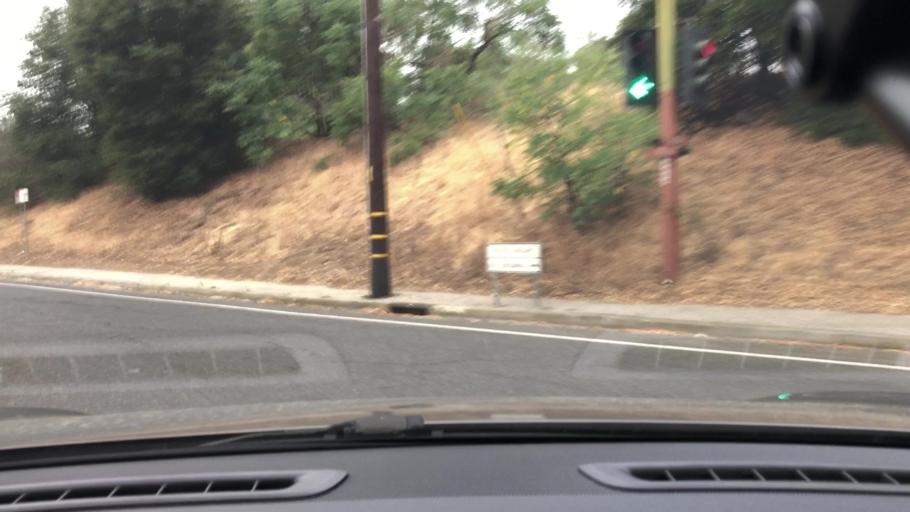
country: US
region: California
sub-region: Santa Clara County
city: Monte Sereno
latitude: 37.2629
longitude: -121.9925
